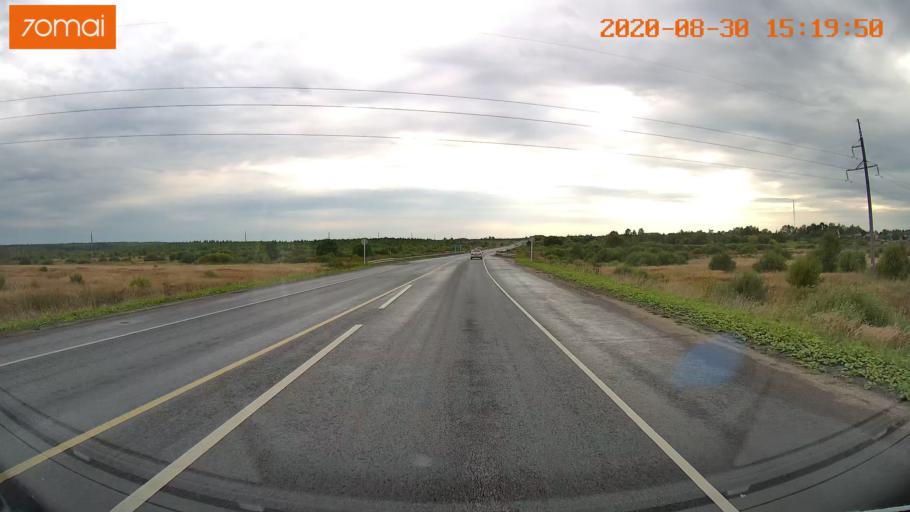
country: RU
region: Ivanovo
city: Rodniki
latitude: 57.1070
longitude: 41.7783
